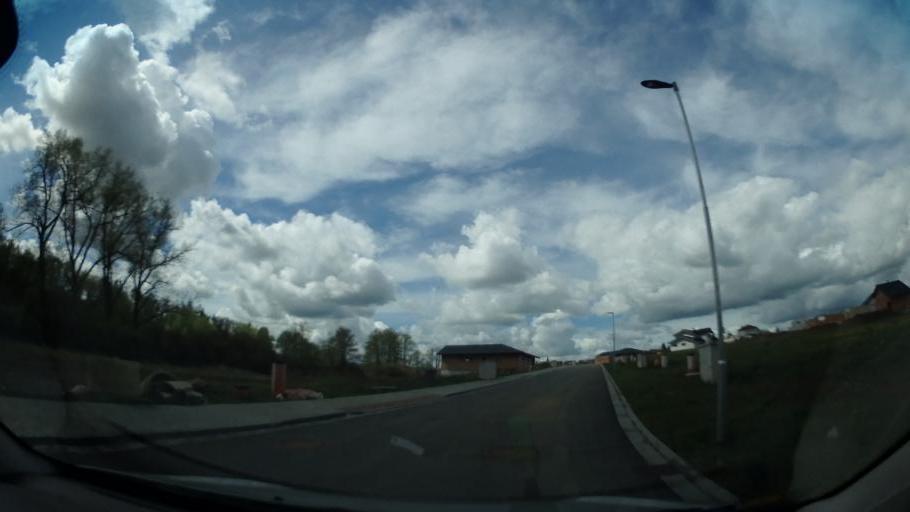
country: CZ
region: Vysocina
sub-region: Okres Zd'ar nad Sazavou
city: Velka Bites
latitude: 49.2910
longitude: 16.2349
